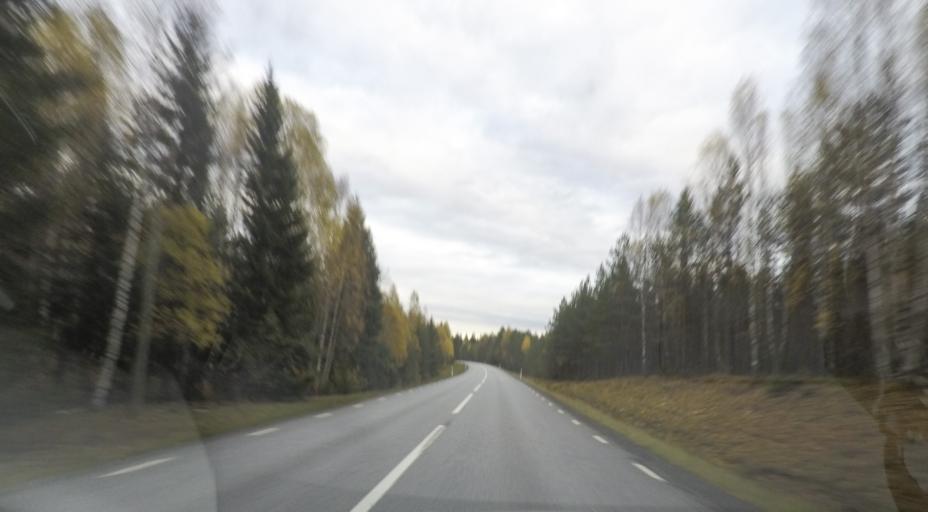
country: SE
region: OErebro
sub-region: Nora Kommun
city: As
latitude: 59.5231
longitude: 14.8374
